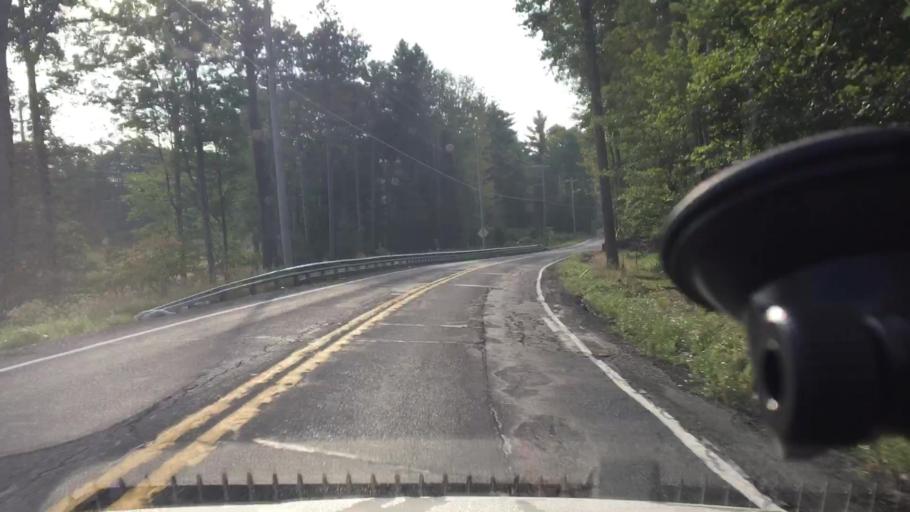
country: US
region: Pennsylvania
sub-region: Monroe County
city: Mount Pocono
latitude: 41.1031
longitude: -75.3534
